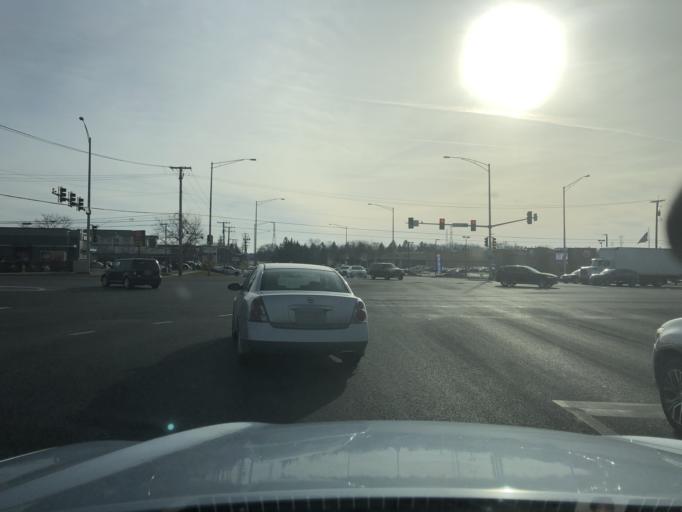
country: US
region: Illinois
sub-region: DuPage County
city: Glendale Heights
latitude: 41.9032
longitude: -88.0819
